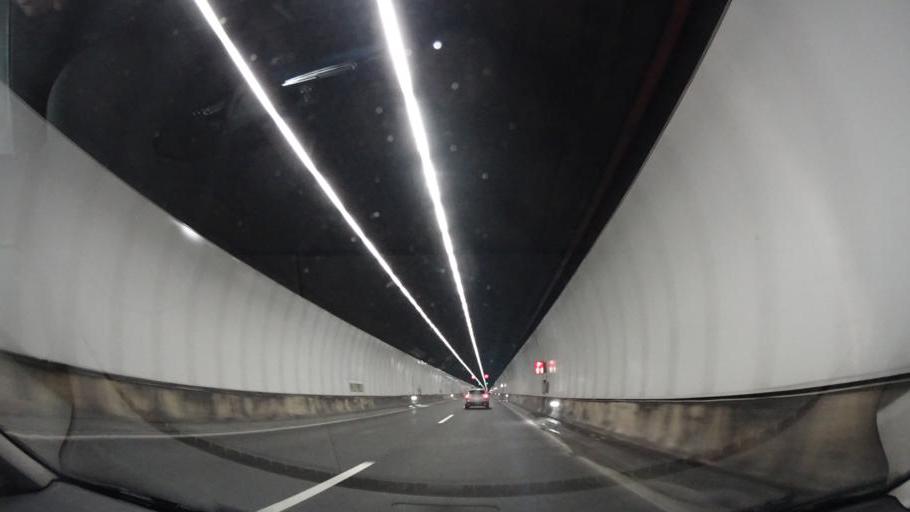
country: ES
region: Basque Country
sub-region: Bizkaia
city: Basauri
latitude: 43.2324
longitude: -2.8970
